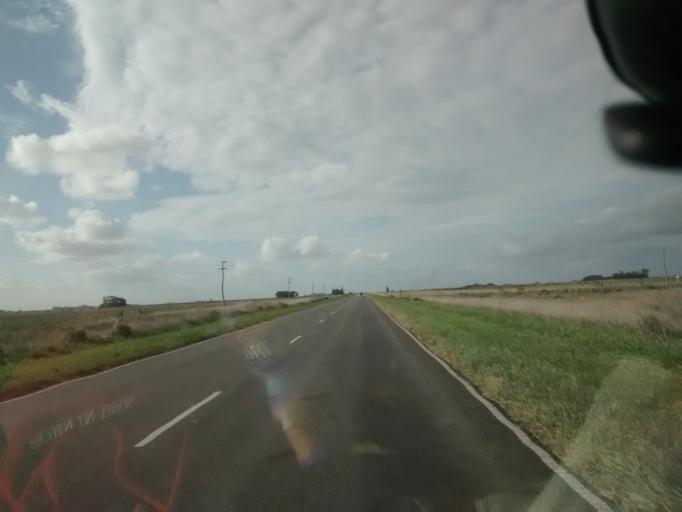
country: AR
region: Buenos Aires
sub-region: Partido de Ayacucho
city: Ayacucho
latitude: -37.0419
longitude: -58.5410
